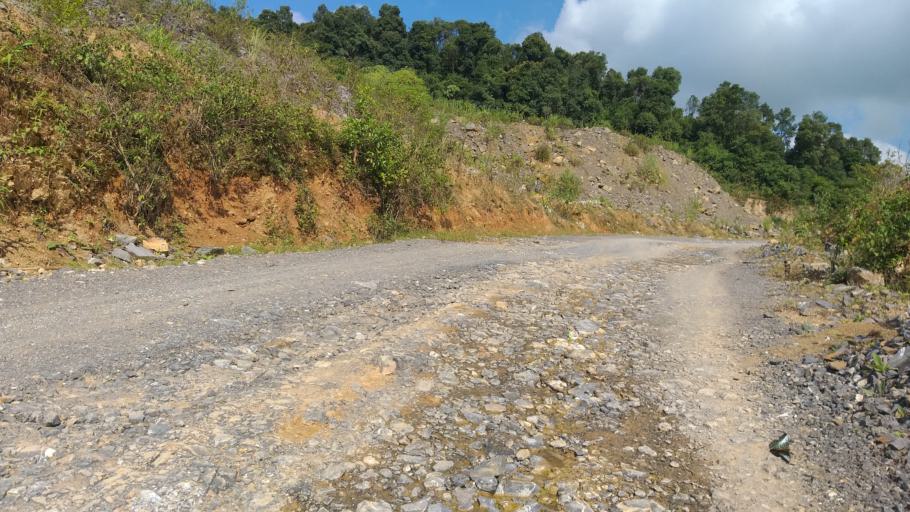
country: LA
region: Phongsali
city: Khoa
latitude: 21.2209
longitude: 102.5980
